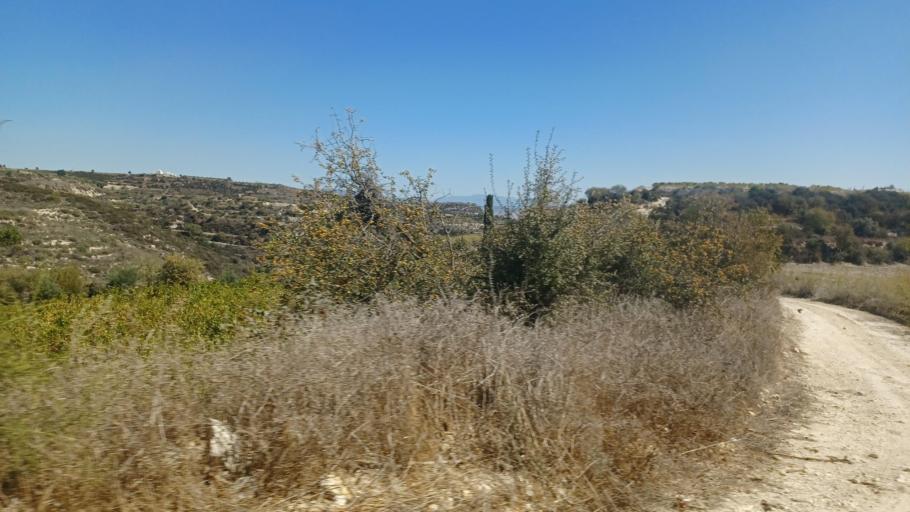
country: CY
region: Pafos
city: Mesogi
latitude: 34.8253
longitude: 32.4804
